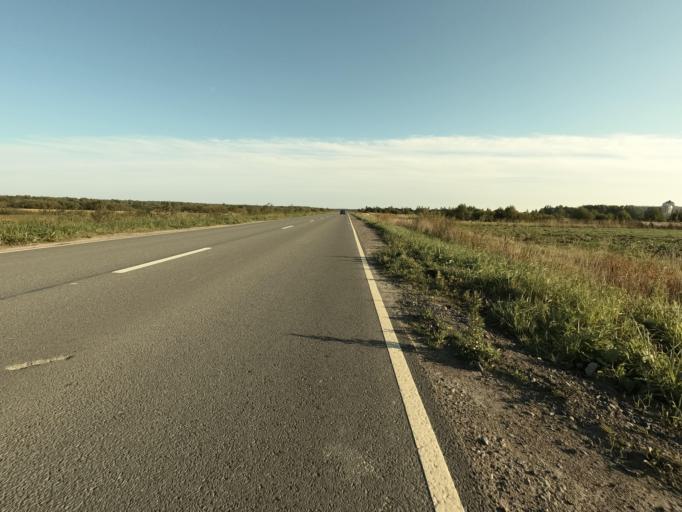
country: RU
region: St.-Petersburg
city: Sapernyy
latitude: 59.7497
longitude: 30.6393
